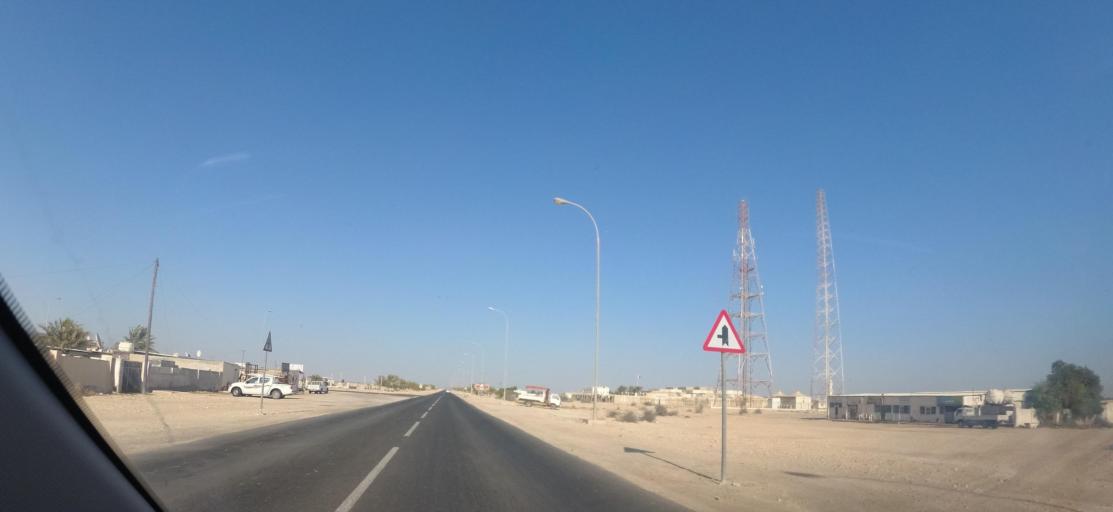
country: QA
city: Al Ghuwayriyah
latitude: 25.8287
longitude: 51.2483
